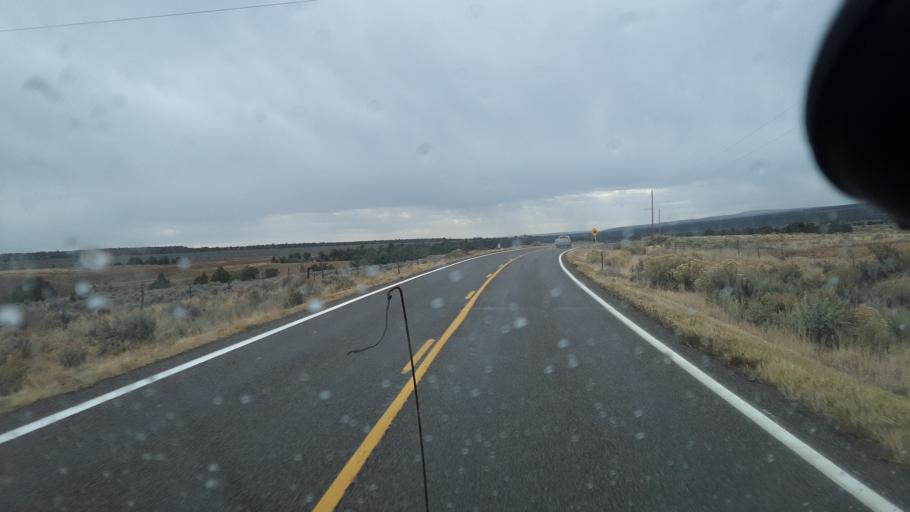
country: US
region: New Mexico
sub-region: San Juan County
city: Spencerville
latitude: 37.0628
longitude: -108.1748
